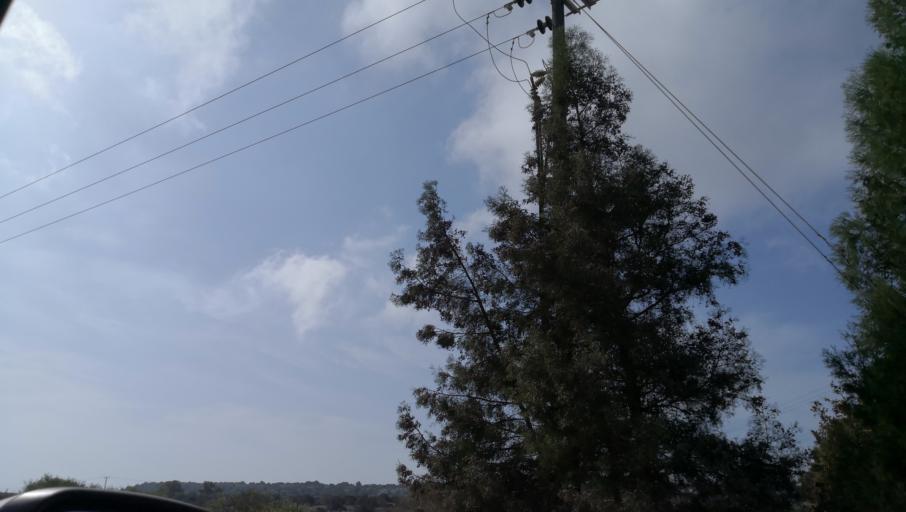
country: CY
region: Ammochostos
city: Protaras
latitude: 35.0138
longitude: 34.0323
